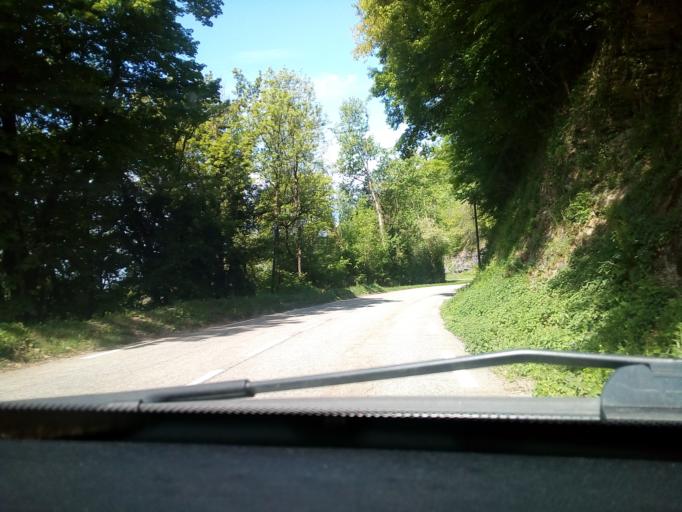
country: FR
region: Rhone-Alpes
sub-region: Departement de l'Isere
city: Le Champ-pres-Froges
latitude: 45.2700
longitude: 5.9526
